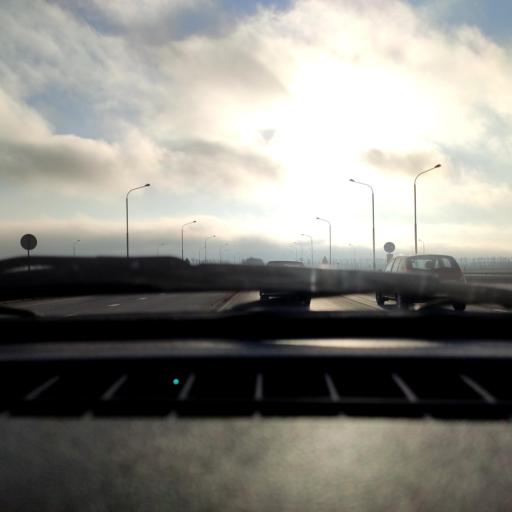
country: RU
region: Bashkortostan
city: Chishmy
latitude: 54.6673
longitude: 55.3999
